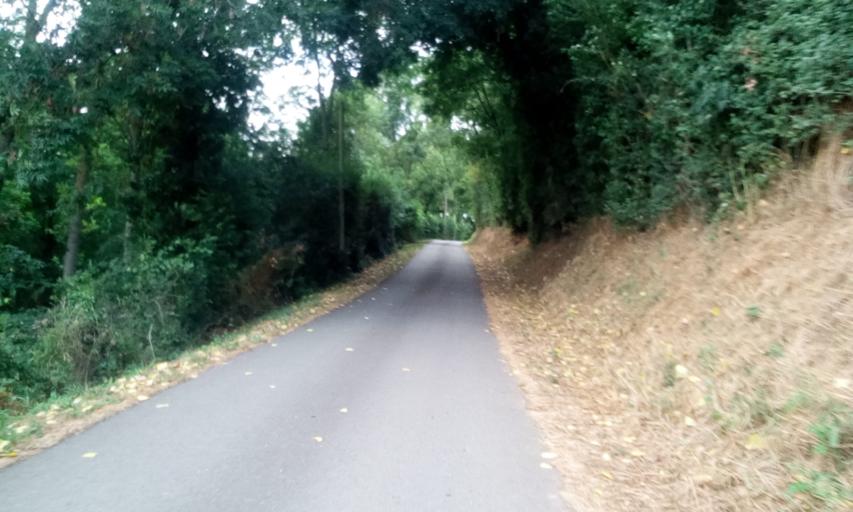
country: FR
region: Lower Normandy
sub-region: Departement du Calvados
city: Thury-Harcourt
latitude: 48.9920
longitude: -0.4154
